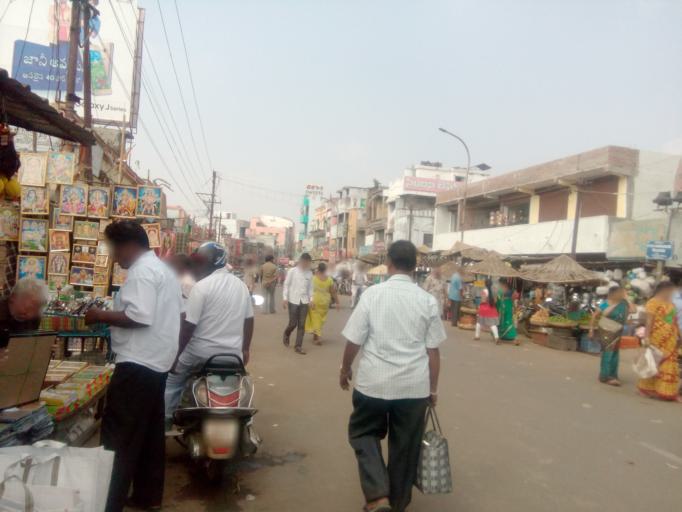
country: IN
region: Andhra Pradesh
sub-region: Vizianagaram District
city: Vizianagaram
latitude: 18.1155
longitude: 83.4094
